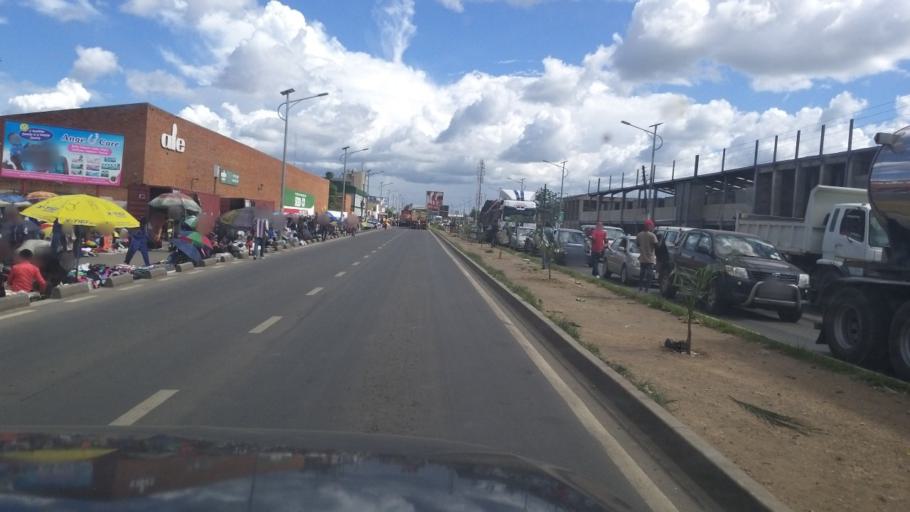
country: ZM
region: Lusaka
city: Lusaka
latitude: -15.4226
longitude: 28.2785
